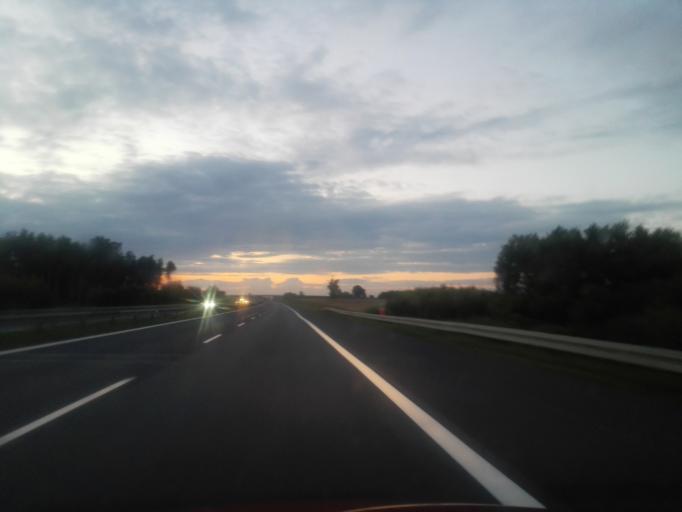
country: PL
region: Lodz Voivodeship
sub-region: Piotrkow Trybunalski
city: Piotrkow Trybunalski
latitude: 51.4502
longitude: 19.6416
